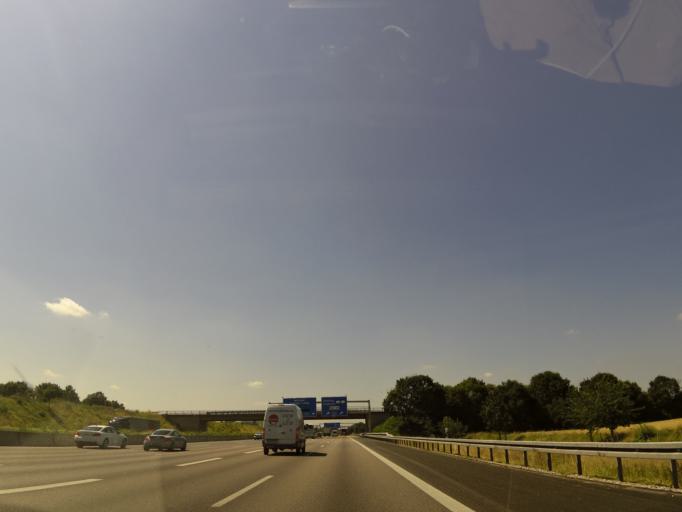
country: DE
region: Bavaria
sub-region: Upper Bavaria
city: Garching bei Munchen
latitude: 48.2347
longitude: 11.6358
